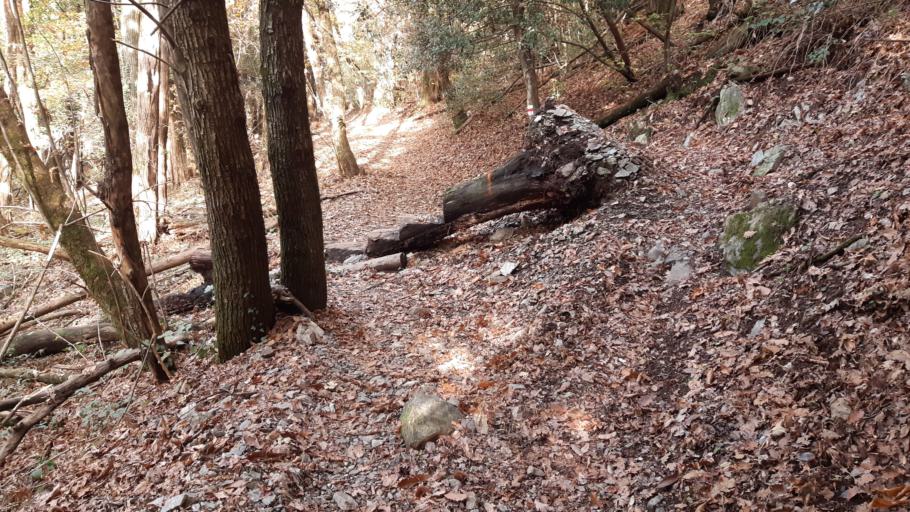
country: IT
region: Lombardy
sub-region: Provincia di Varese
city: Brusimpiano
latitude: 45.9442
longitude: 8.9072
